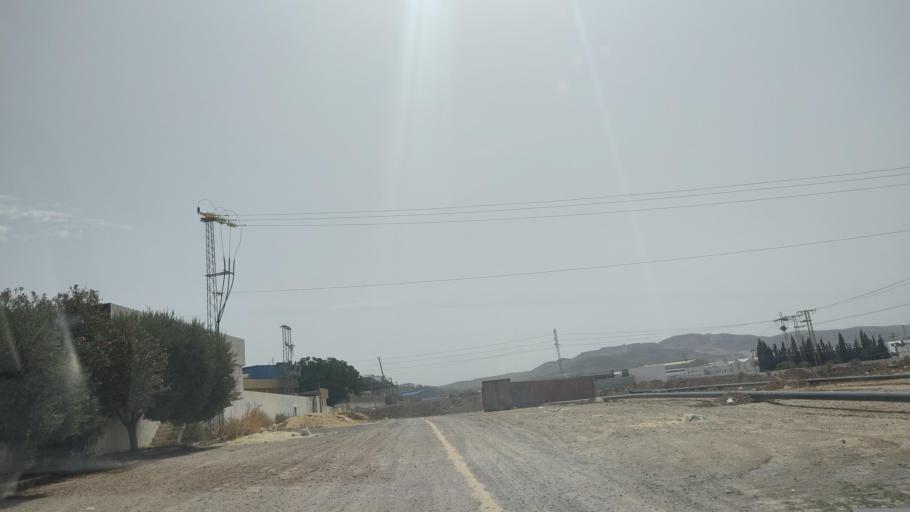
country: TN
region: Tunis
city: La Mohammedia
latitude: 36.5604
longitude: 10.0824
